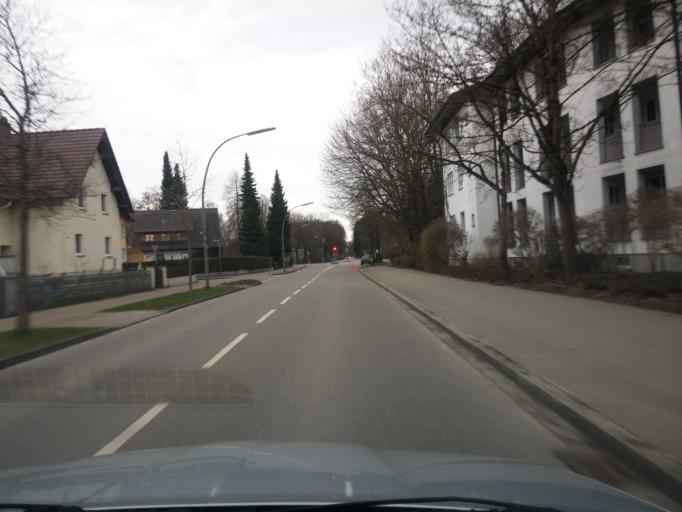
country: DE
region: Bavaria
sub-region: Swabia
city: Memmingen
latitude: 47.9834
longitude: 10.1969
